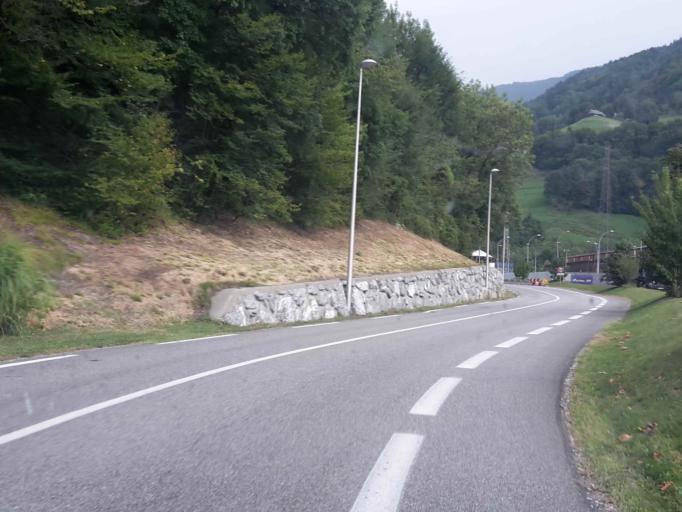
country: FR
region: Rhone-Alpes
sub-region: Departement de la Savoie
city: Ugine
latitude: 45.7473
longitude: 6.4273
